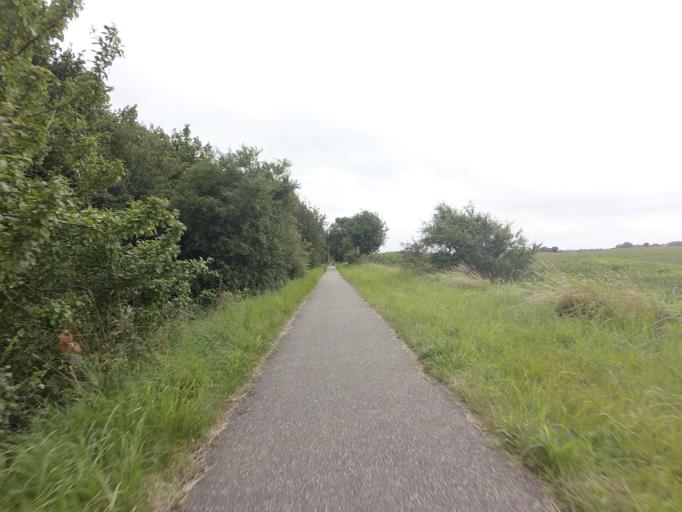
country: DK
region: Central Jutland
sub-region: Horsens Kommune
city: Braedstrup
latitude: 56.0056
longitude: 9.5874
